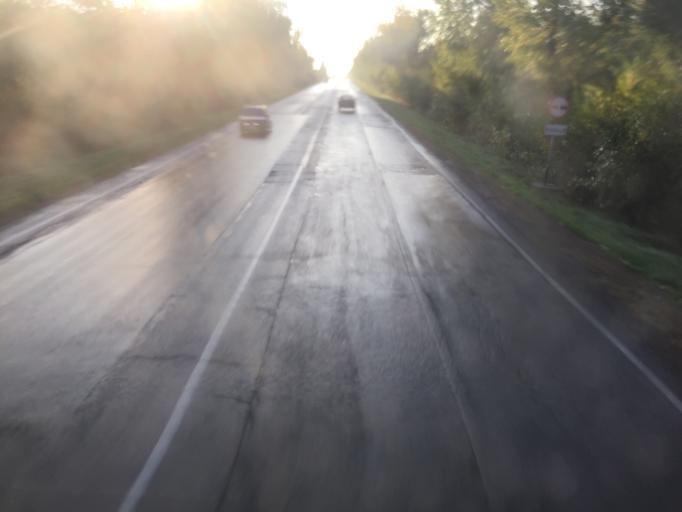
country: RU
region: Rostov
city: Kirovskaya
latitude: 47.0251
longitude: 39.8900
